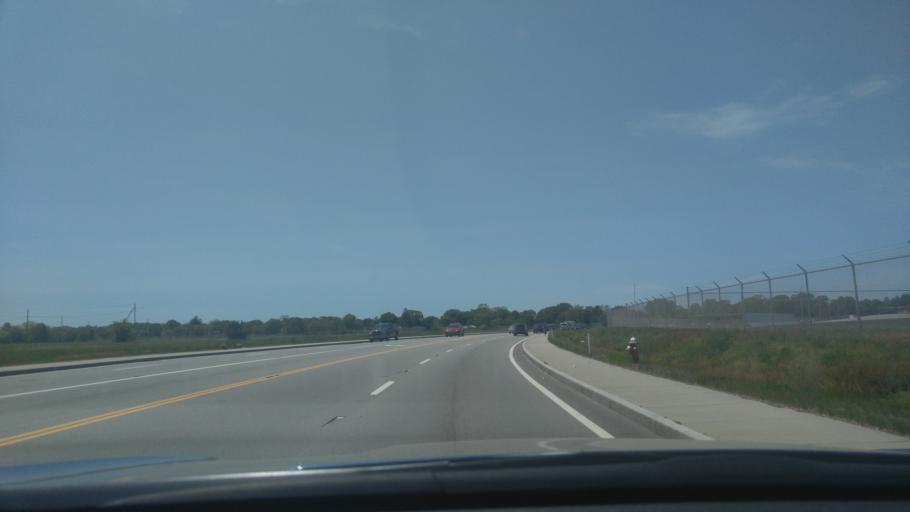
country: US
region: Rhode Island
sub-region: Kent County
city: Warwick
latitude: 41.7079
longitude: -71.4368
